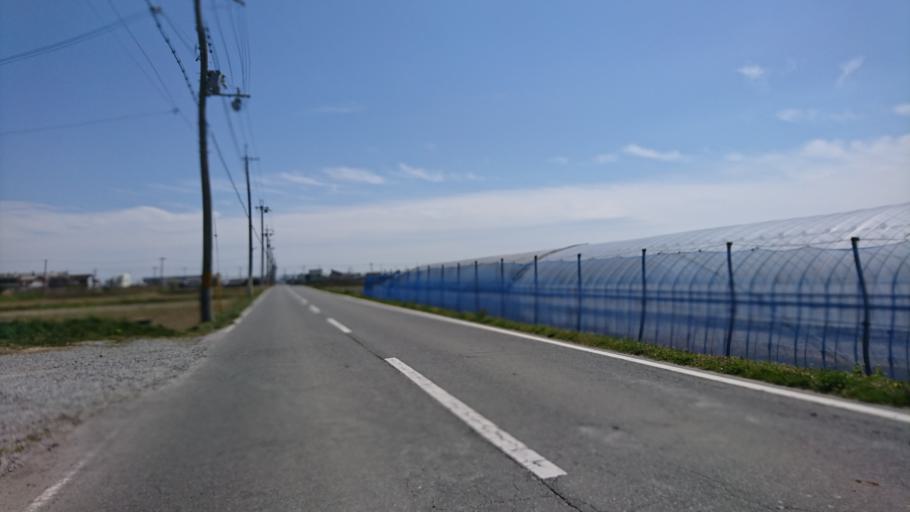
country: JP
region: Hyogo
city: Kakogawacho-honmachi
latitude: 34.7474
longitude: 134.8889
